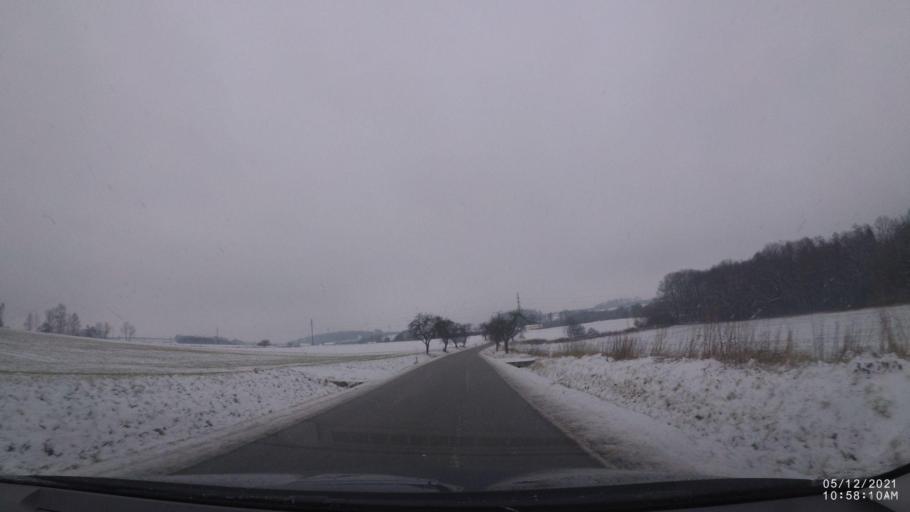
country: CZ
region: Kralovehradecky
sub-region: Okres Rychnov nad Kneznou
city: Rychnov nad Kneznou
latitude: 50.1638
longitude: 16.2510
